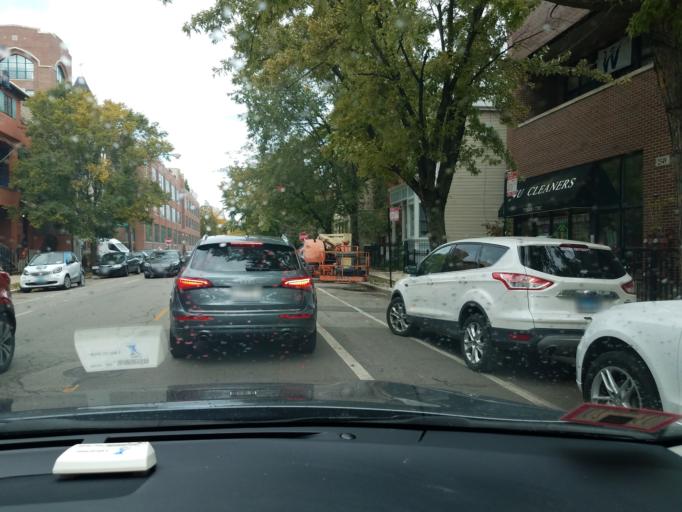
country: US
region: Illinois
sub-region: Cook County
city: Chicago
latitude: 41.9283
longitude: -87.6634
